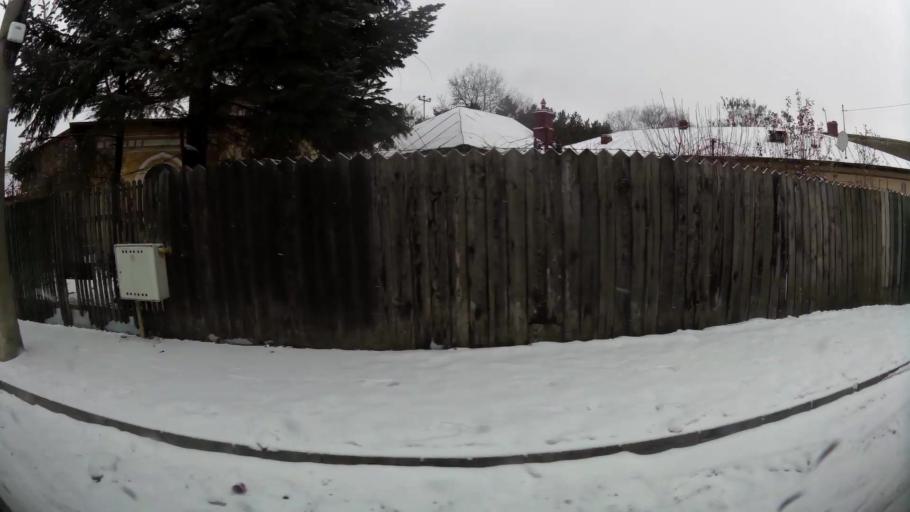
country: RO
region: Prahova
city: Ploiesti
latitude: 44.9317
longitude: 26.0158
